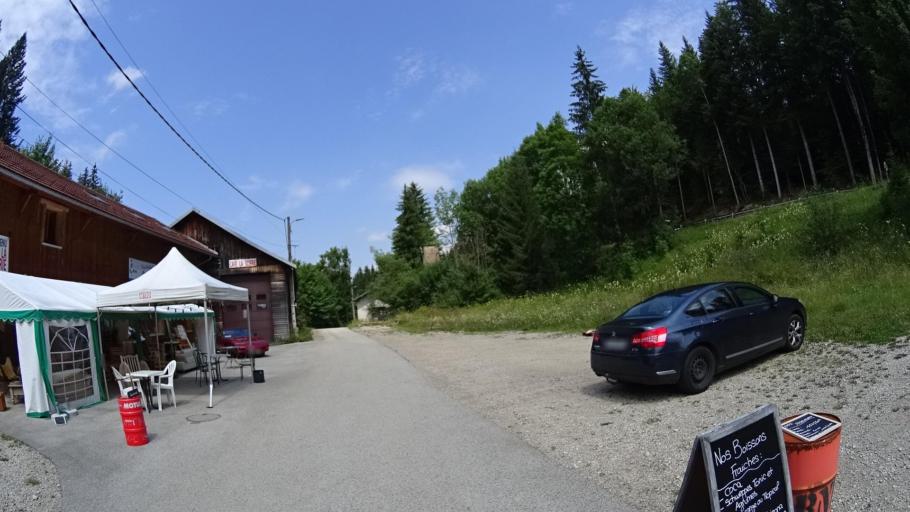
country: FR
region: Franche-Comte
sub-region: Departement du Doubs
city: Les Fourgs
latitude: 46.8114
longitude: 6.3217
